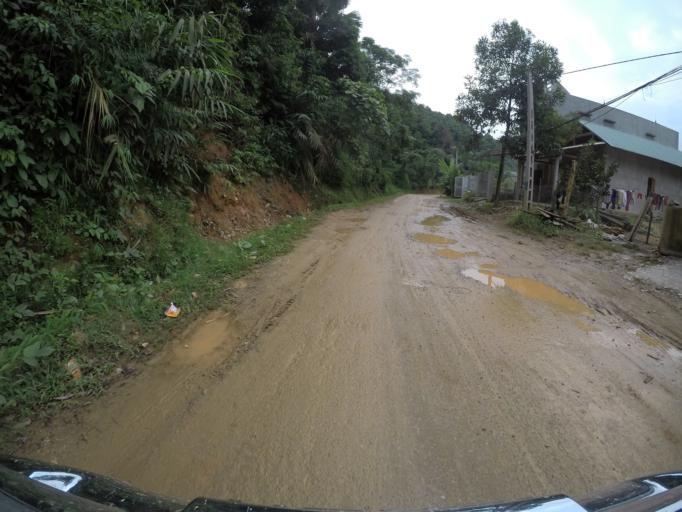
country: VN
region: Yen Bai
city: Co Phuc
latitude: 21.8439
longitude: 104.6171
